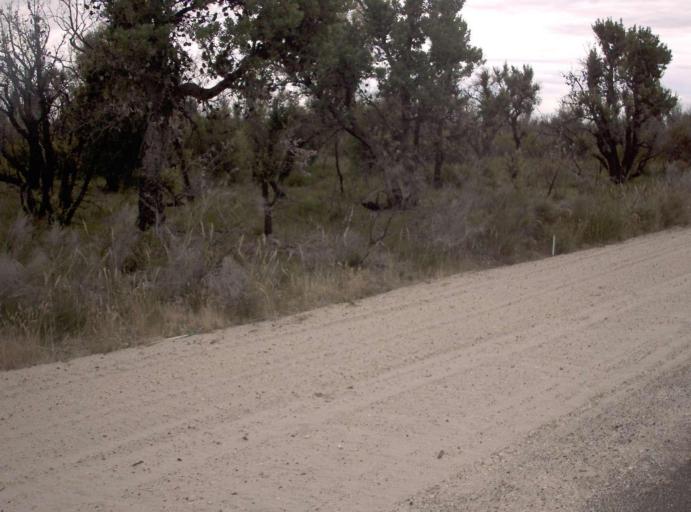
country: AU
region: Victoria
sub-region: East Gippsland
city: Bairnsdale
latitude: -38.1169
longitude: 147.4608
